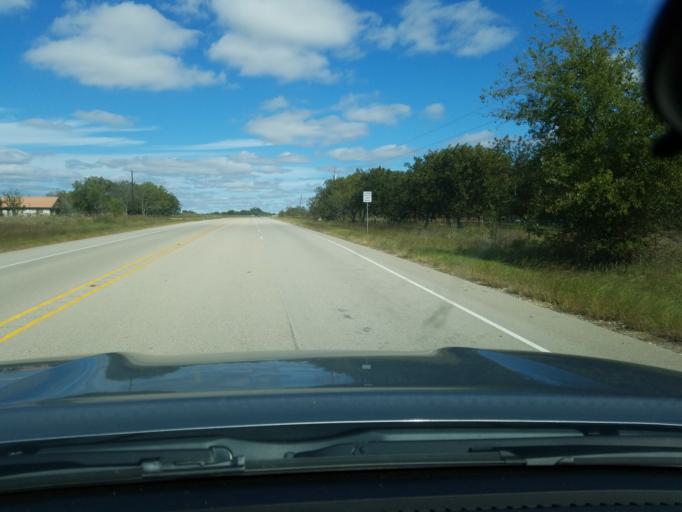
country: US
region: Texas
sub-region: Hamilton County
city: Hamilton
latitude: 31.6448
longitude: -98.1482
